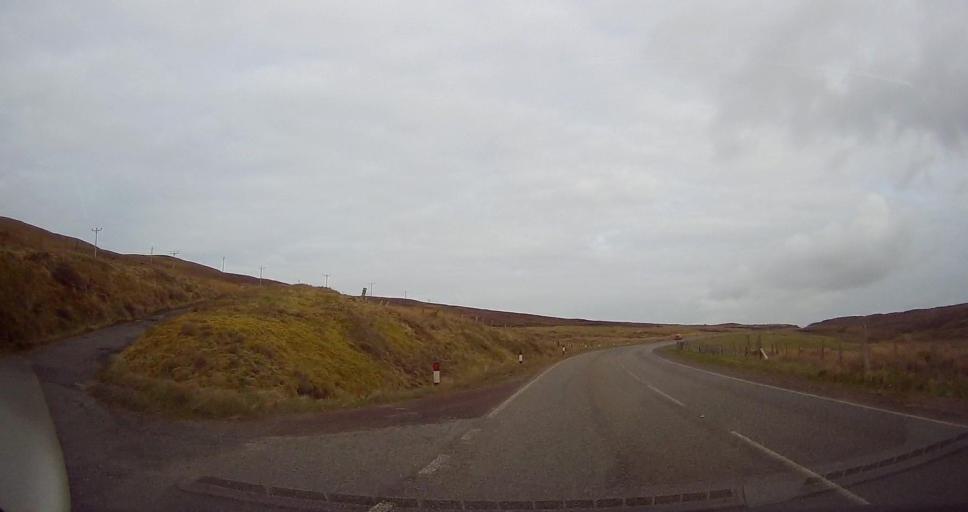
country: GB
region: Scotland
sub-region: Shetland Islands
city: Sandwick
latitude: 60.0840
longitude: -1.2317
